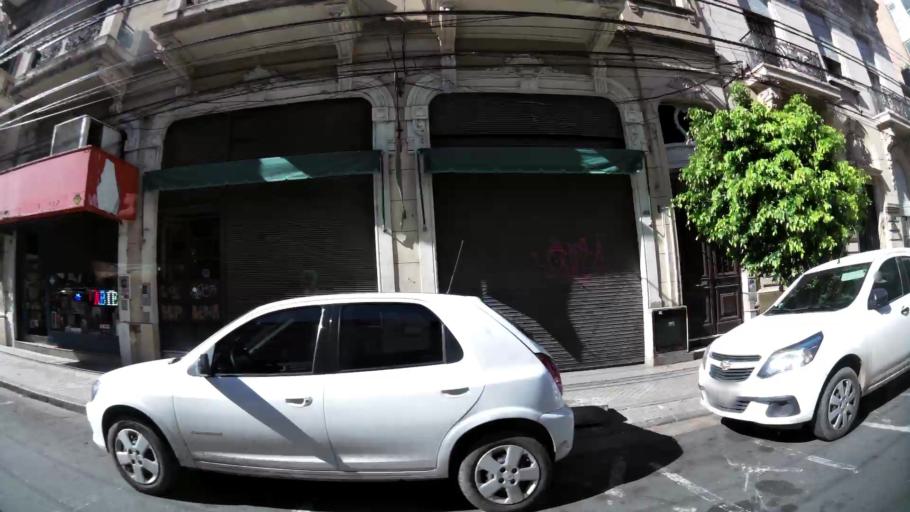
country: AR
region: Santa Fe
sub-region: Departamento de Rosario
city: Rosario
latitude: -32.9515
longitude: -60.6402
